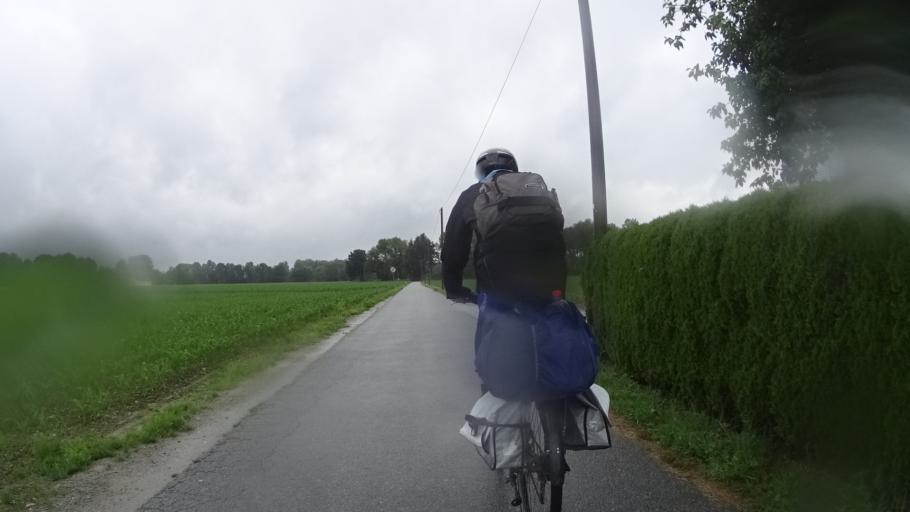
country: DE
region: Bavaria
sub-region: Lower Bavaria
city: Pocking
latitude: 48.4360
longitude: 13.3697
